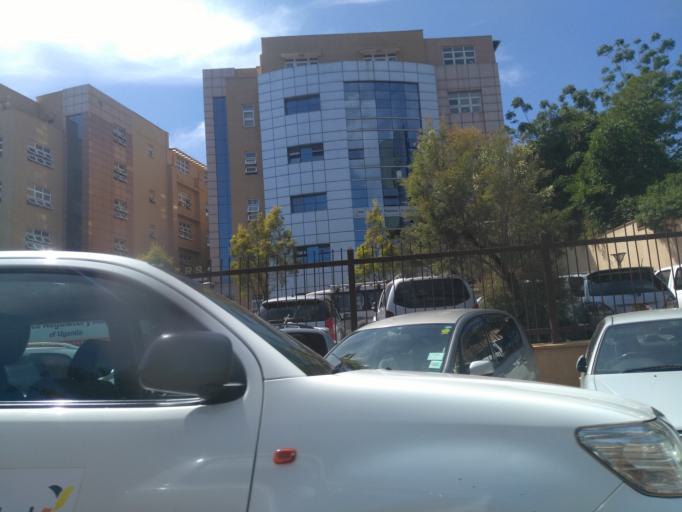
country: UG
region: Central Region
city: Kampala Central Division
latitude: 0.3307
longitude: 32.5780
